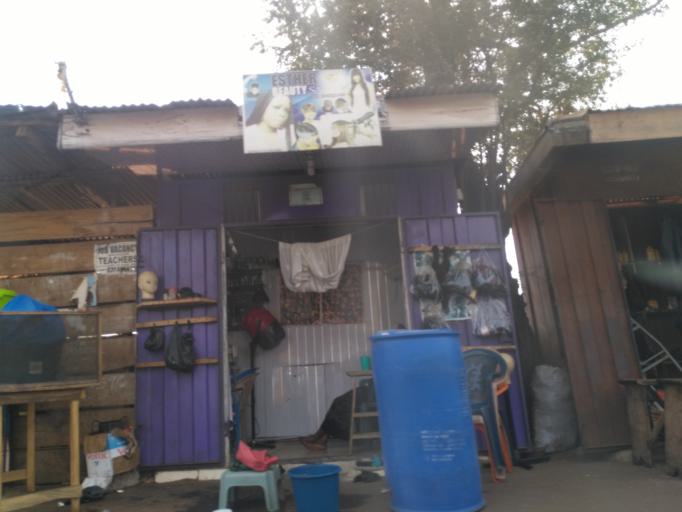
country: GH
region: Ashanti
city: Kumasi
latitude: 6.7010
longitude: -1.6084
